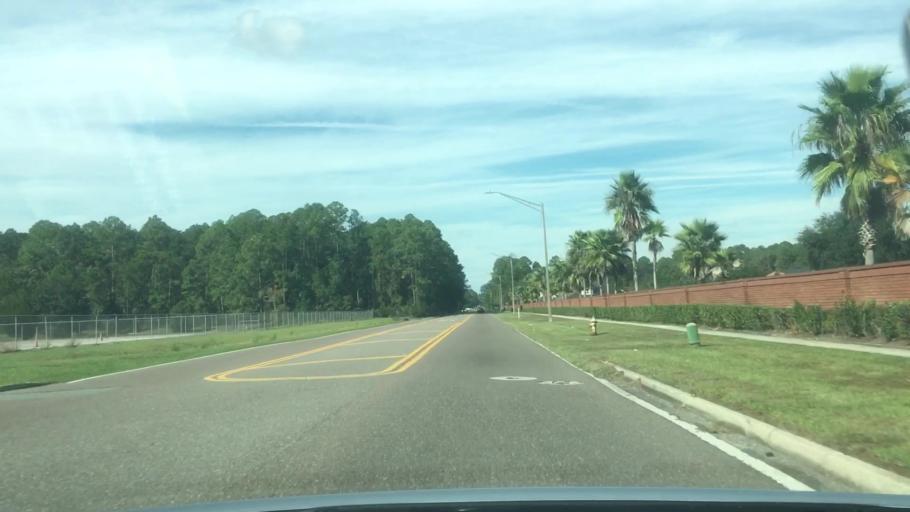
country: US
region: Florida
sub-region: Nassau County
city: Yulee
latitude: 30.4847
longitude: -81.6088
